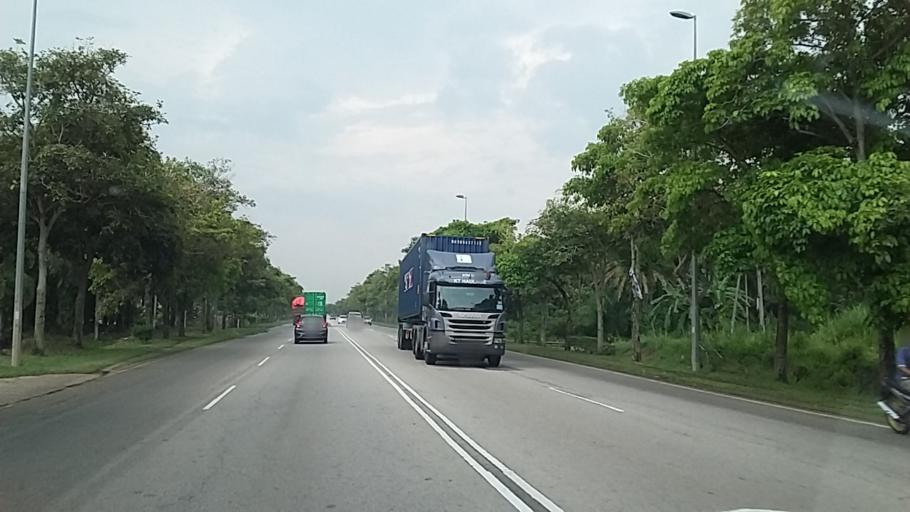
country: MY
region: Johor
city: Parit Raja
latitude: 1.8728
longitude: 103.1344
